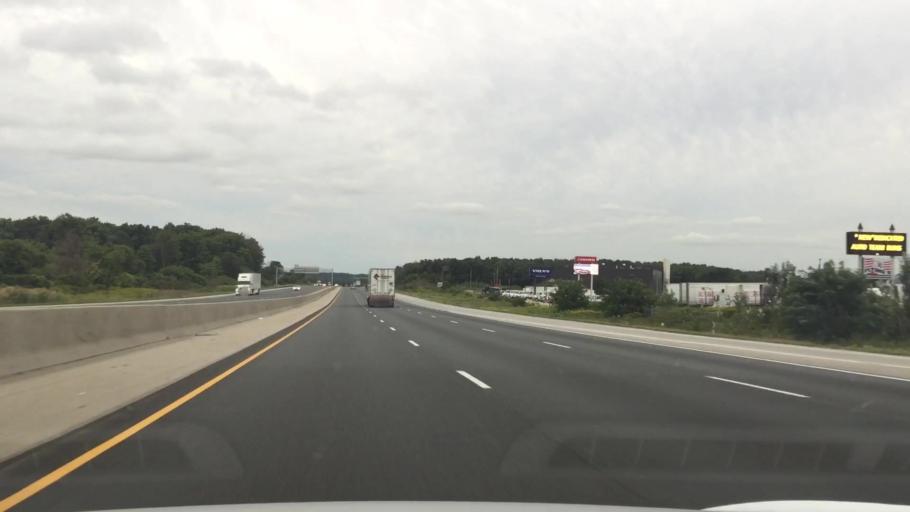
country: CA
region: Ontario
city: Kitchener
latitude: 43.3268
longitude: -80.4537
